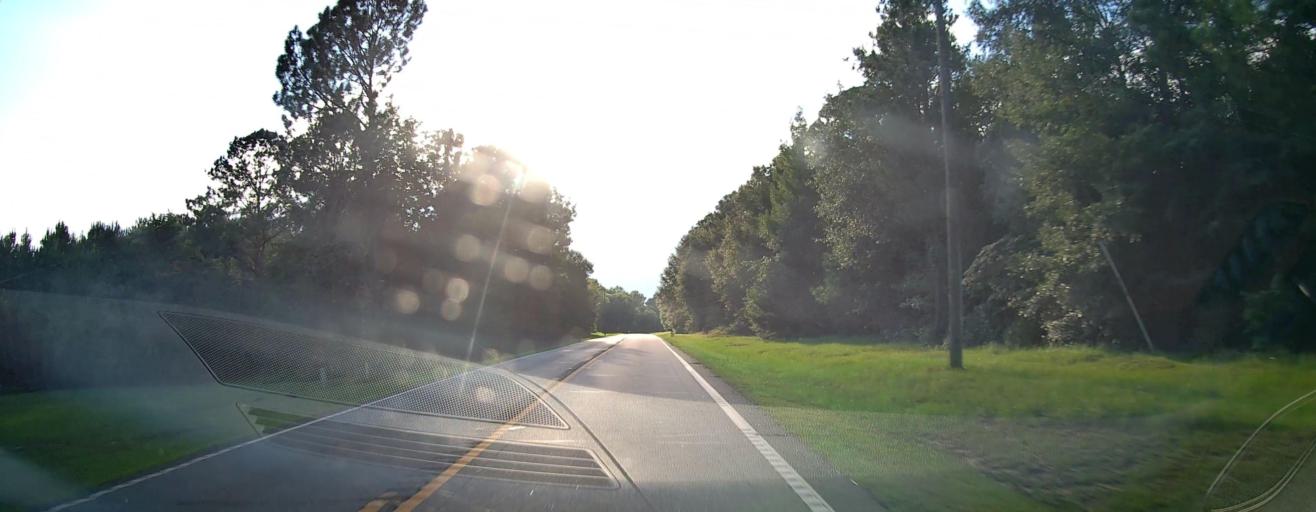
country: US
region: Georgia
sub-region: Pulaski County
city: Hawkinsville
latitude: 32.2670
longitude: -83.5341
